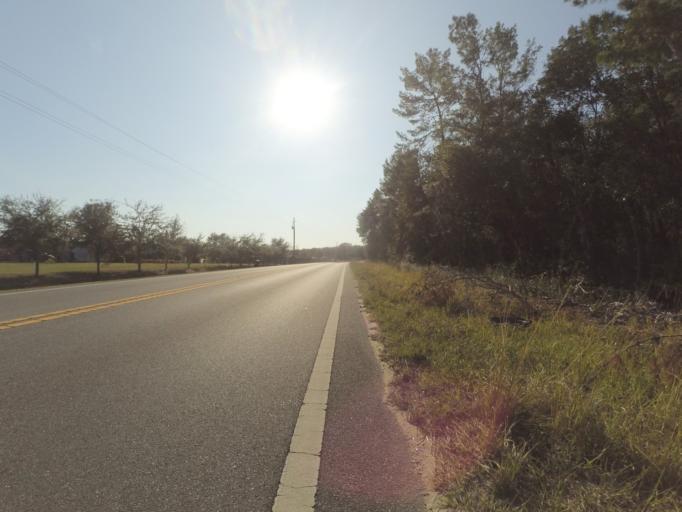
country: US
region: Florida
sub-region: Lake County
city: Umatilla
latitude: 28.9857
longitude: -81.7364
